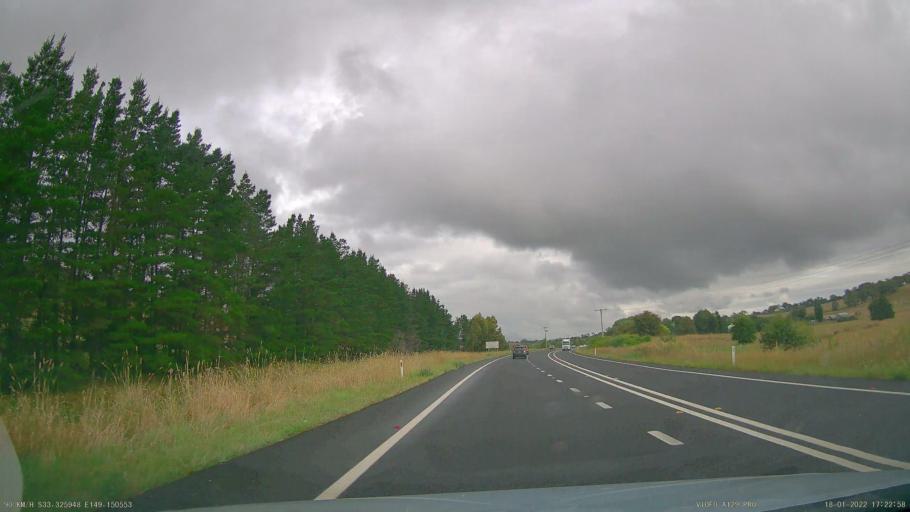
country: AU
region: New South Wales
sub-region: Orange Municipality
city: Orange
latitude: -33.3261
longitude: 149.1507
